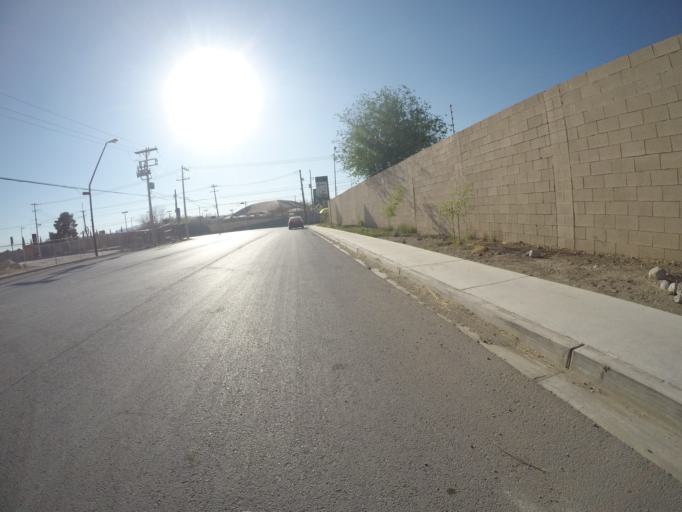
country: US
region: Texas
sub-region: El Paso County
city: Socorro
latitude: 31.6999
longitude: -106.3877
